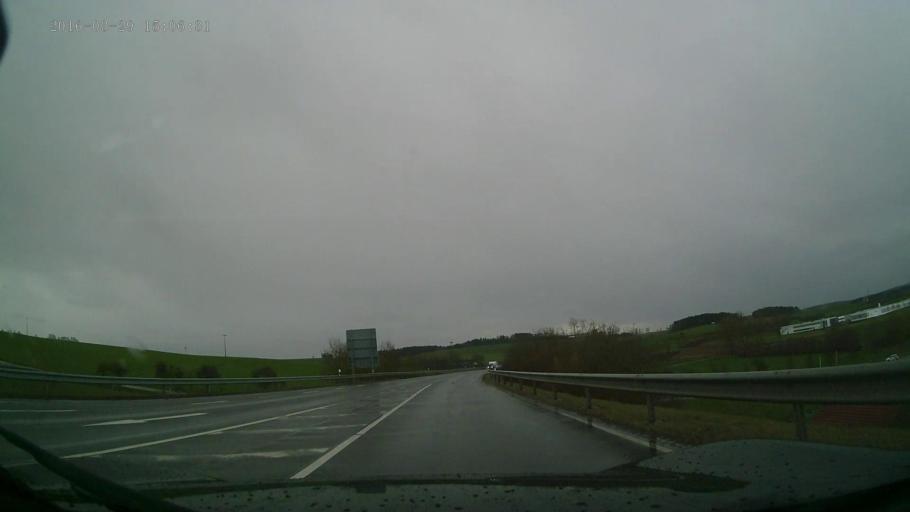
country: DE
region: Baden-Wuerttemberg
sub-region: Karlsruhe Region
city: Buchen
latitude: 49.5134
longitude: 9.3312
